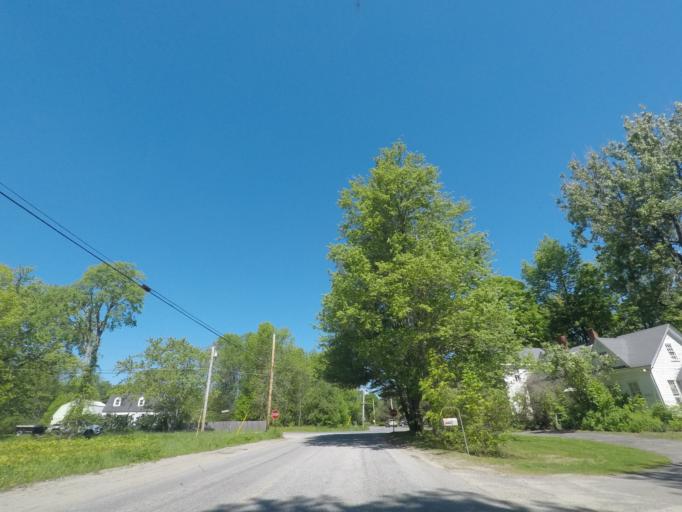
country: US
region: Maine
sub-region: Kennebec County
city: Manchester
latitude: 44.2357
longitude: -69.8866
